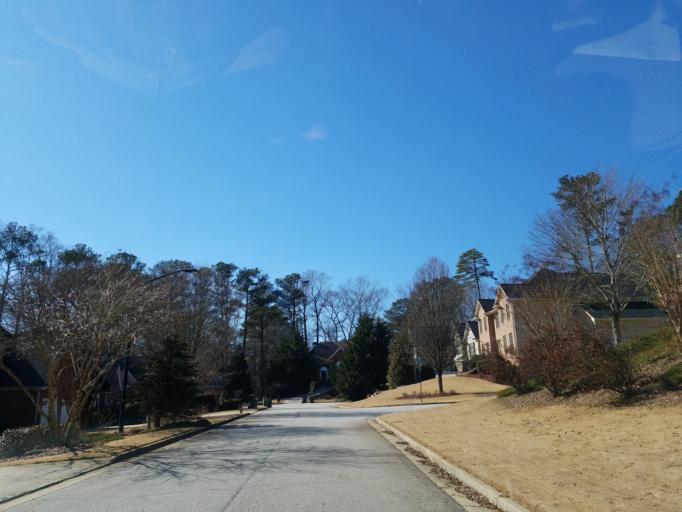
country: US
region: Georgia
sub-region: Fulton County
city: Sandy Springs
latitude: 33.9651
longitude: -84.4589
